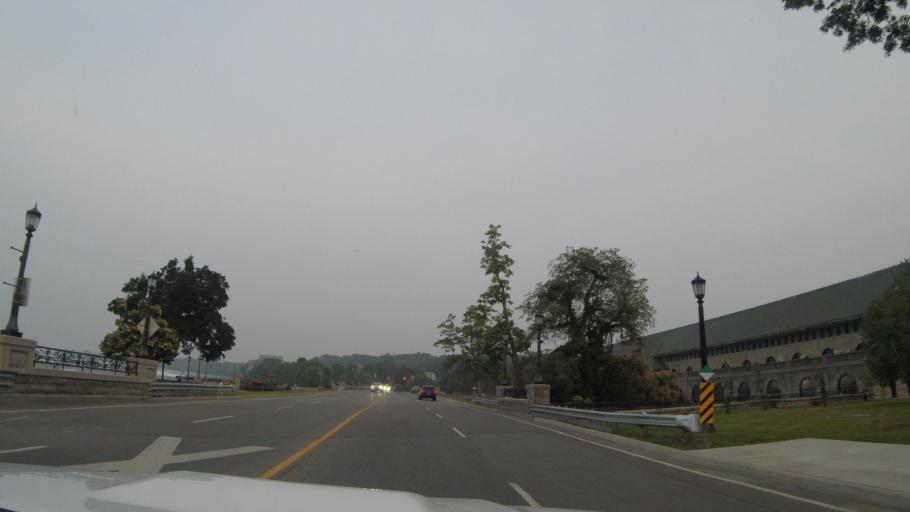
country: CA
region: Ontario
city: Niagara Falls
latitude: 43.0759
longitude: -79.0789
